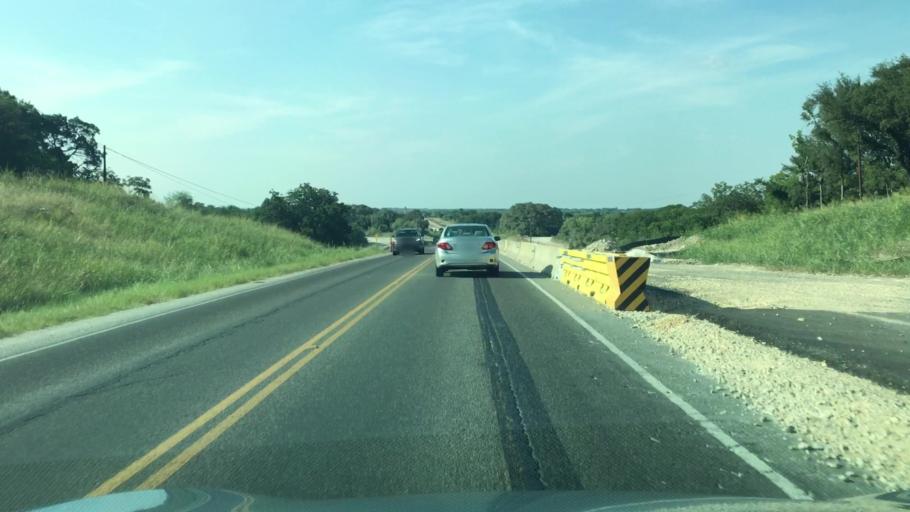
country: US
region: Texas
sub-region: Hays County
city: Buda
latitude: 30.0570
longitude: -97.8741
